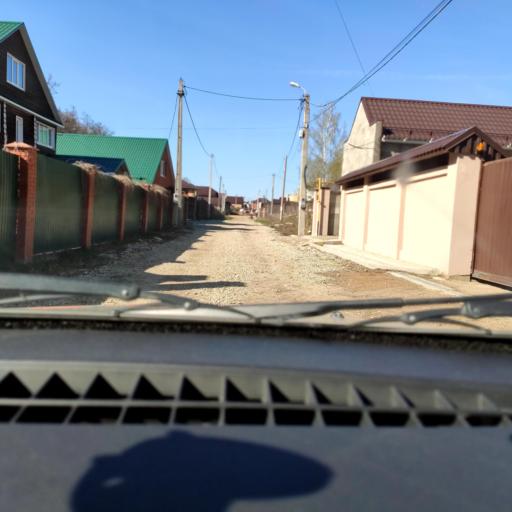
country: RU
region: Bashkortostan
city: Kabakovo
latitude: 54.5964
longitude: 56.1742
